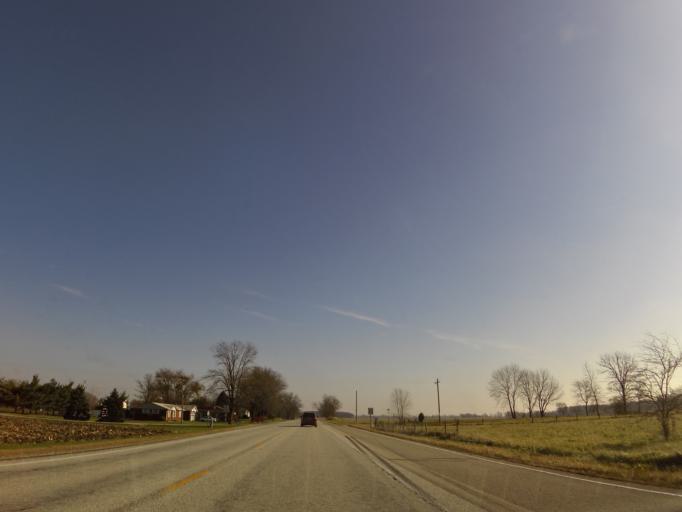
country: US
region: Indiana
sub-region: Shelby County
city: Morristown
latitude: 39.5693
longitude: -85.6280
